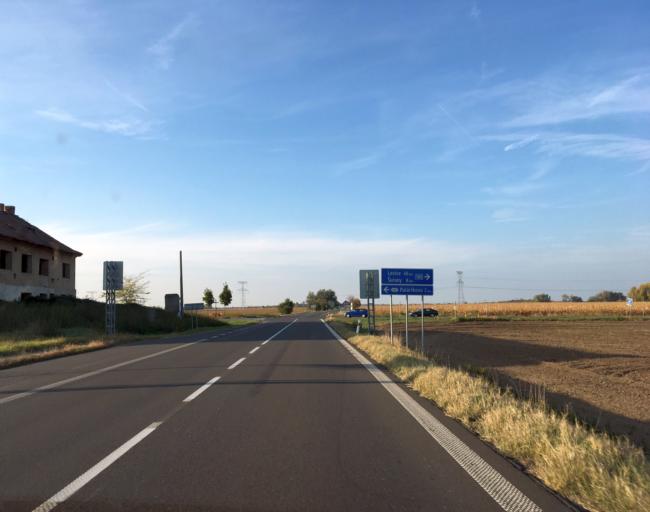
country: SK
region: Nitriansky
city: Surany
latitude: 48.0619
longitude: 18.0999
